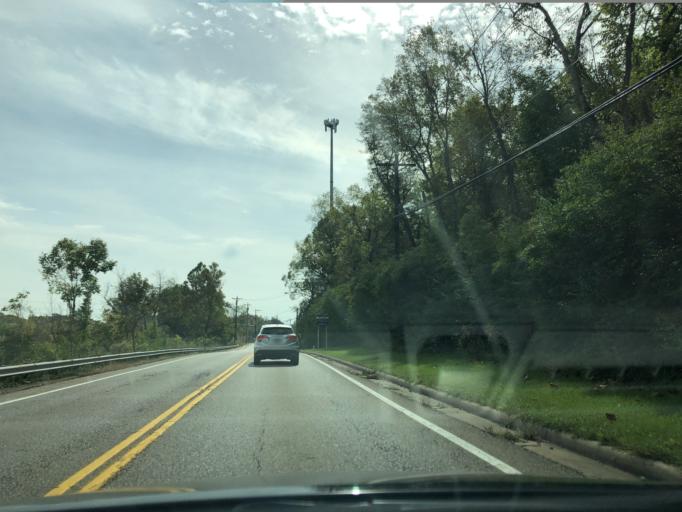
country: US
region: Ohio
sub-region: Clermont County
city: Milford
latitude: 39.1741
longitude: -84.3000
